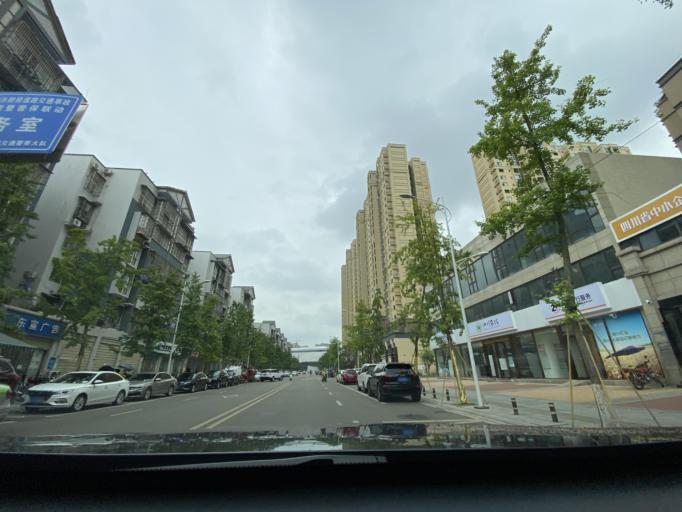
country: CN
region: Sichuan
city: Jiancheng
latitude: 30.4206
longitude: 104.5351
